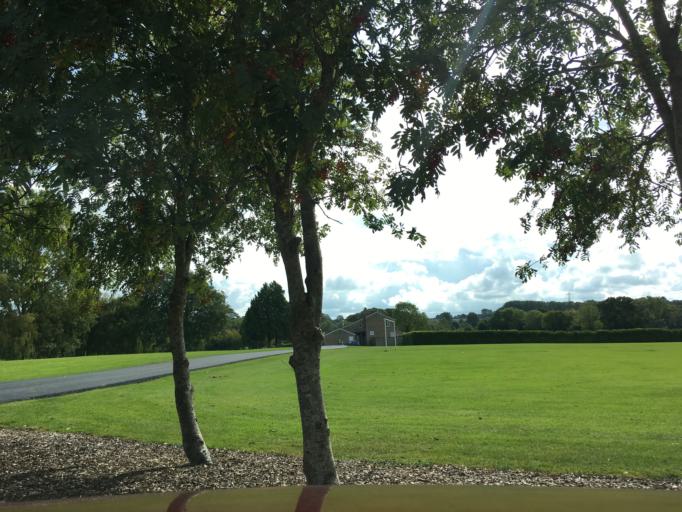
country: GB
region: England
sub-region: South Gloucestershire
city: Thornbury
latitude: 51.6073
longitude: -2.5311
